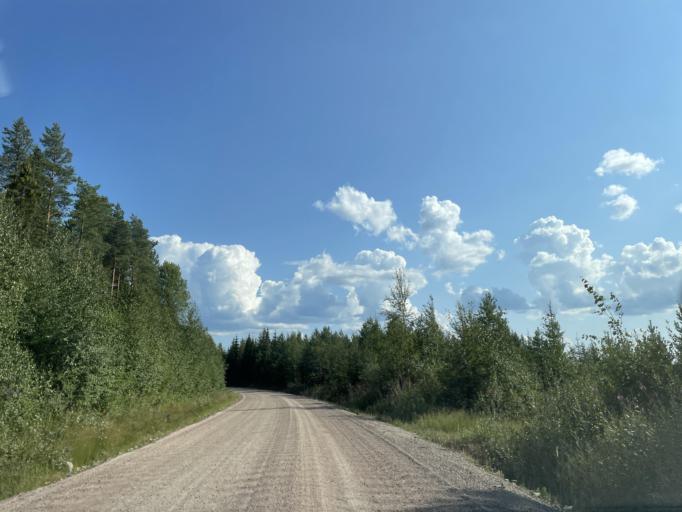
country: FI
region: Central Finland
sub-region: Saarijaervi-Viitasaari
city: Pihtipudas
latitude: 63.3466
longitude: 25.7907
